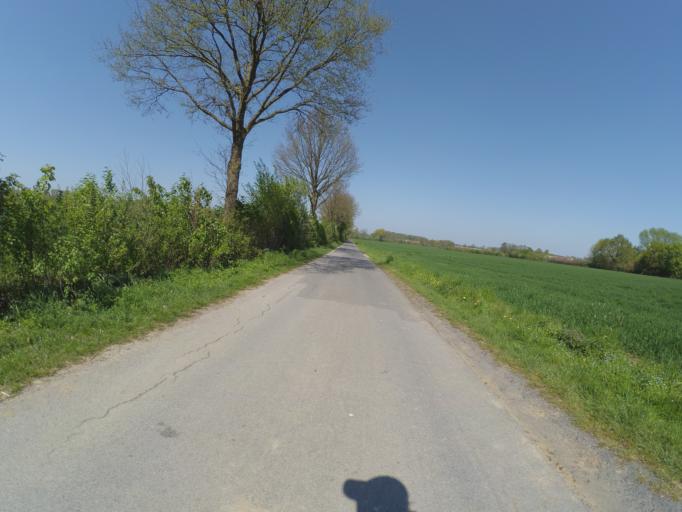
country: DE
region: North Rhine-Westphalia
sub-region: Regierungsbezirk Munster
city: Nordkirchen
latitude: 51.7477
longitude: 7.5476
